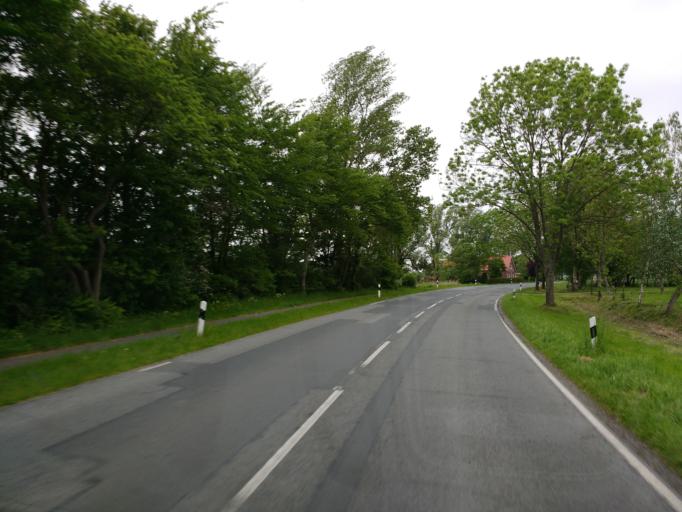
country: DE
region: Lower Saxony
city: Jever
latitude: 53.6283
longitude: 7.9251
